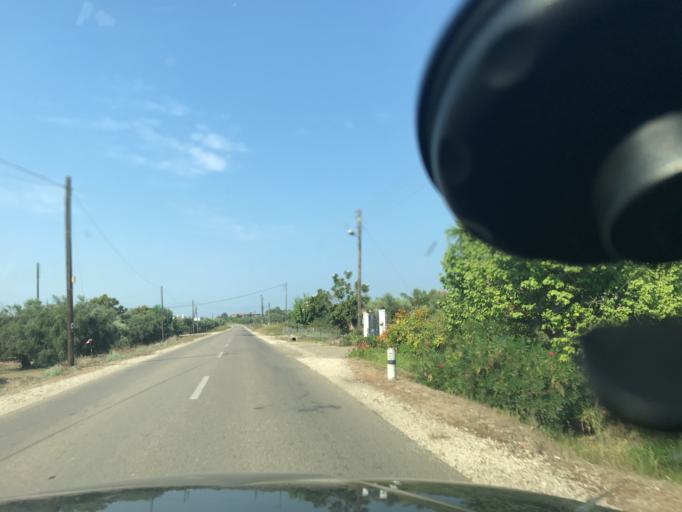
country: GR
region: West Greece
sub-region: Nomos Ileias
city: Kardamas
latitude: 37.7206
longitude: 21.3605
